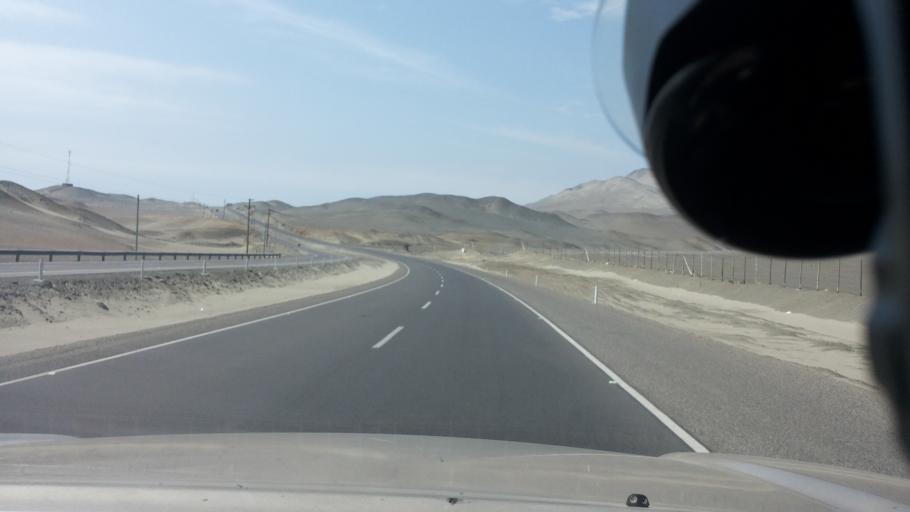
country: PE
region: Ancash
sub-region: Provincia de Huarmey
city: Huarmey
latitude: -10.0166
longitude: -78.1720
